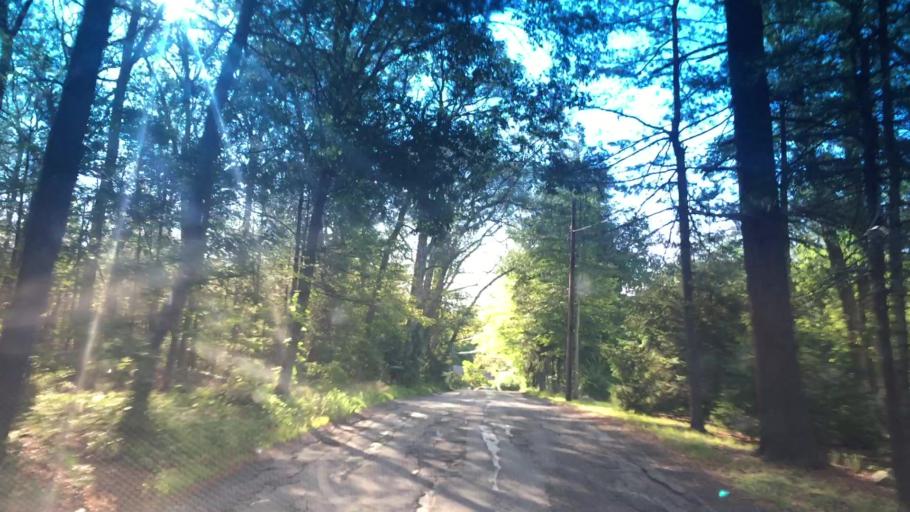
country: US
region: Massachusetts
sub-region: Norfolk County
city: Millis-Clicquot
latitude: 42.1462
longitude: -71.3595
